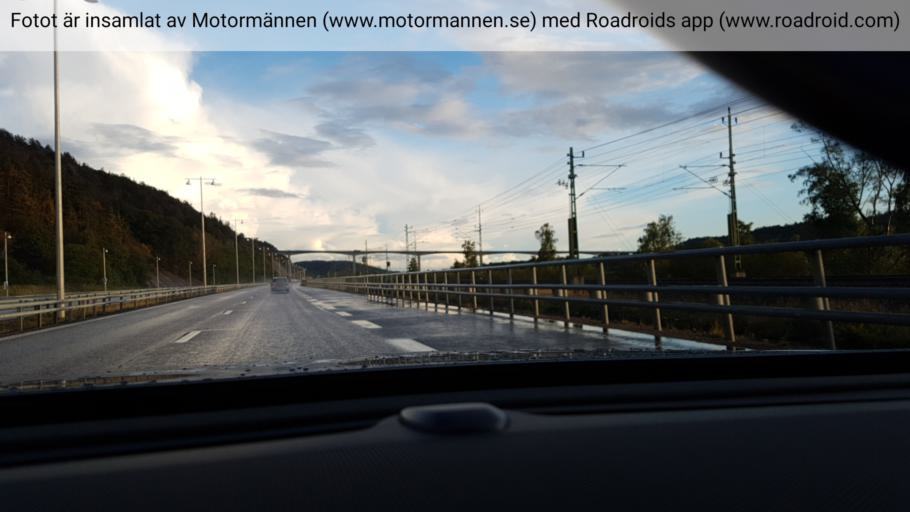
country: SE
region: Vaestra Goetaland
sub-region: Ale Kommun
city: Surte
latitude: 57.8133
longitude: 12.0161
